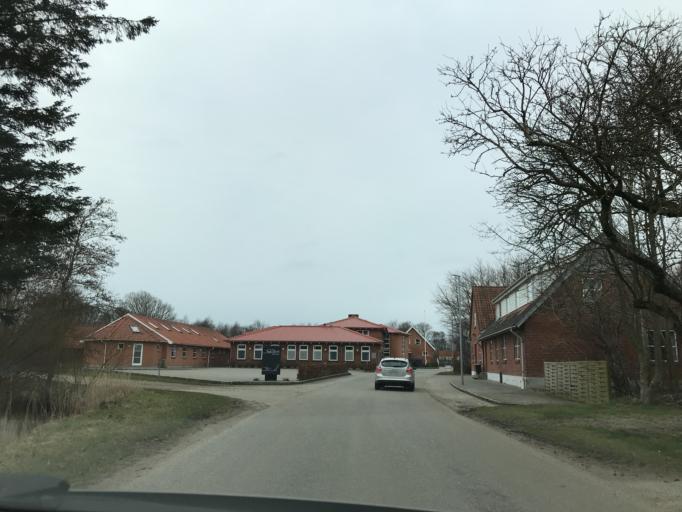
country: DK
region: South Denmark
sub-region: Varde Kommune
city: Oksbol
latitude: 55.8112
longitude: 8.2973
